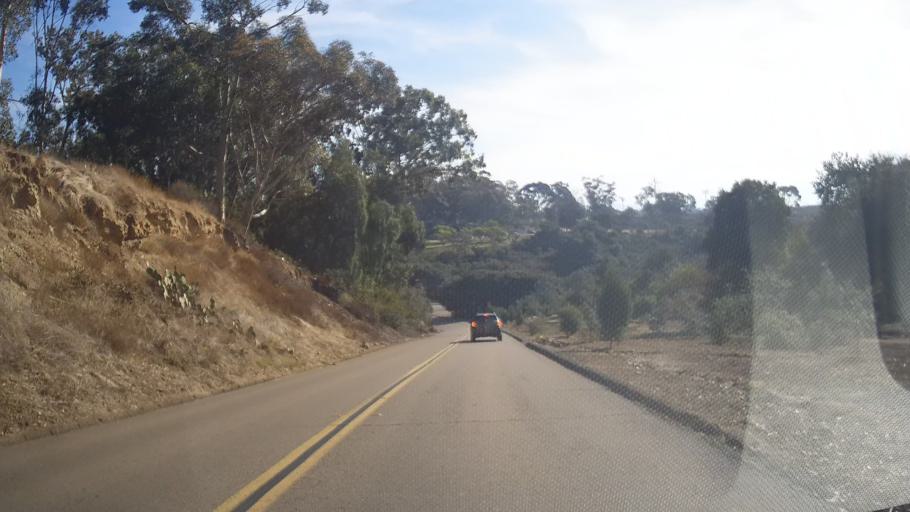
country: US
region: California
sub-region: San Diego County
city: San Diego
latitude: 32.7402
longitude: -117.1459
